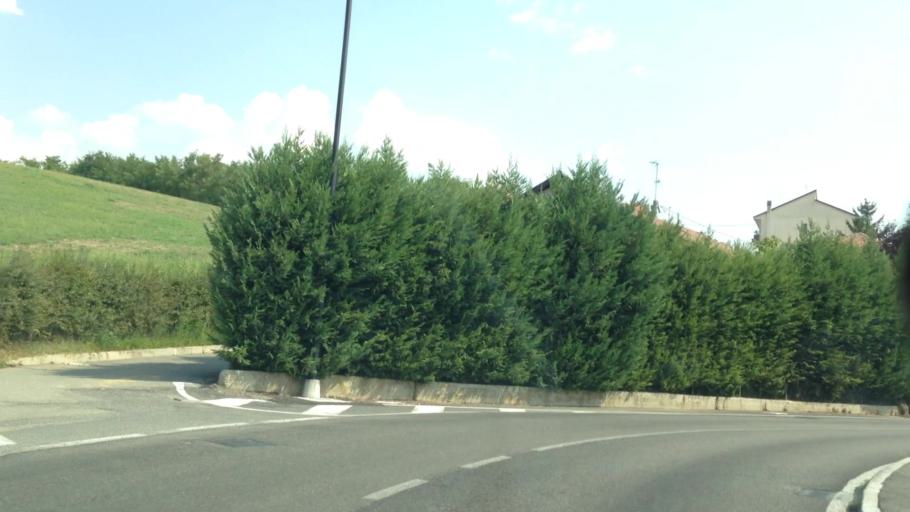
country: IT
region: Piedmont
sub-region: Provincia di Asti
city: Asti
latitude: 44.9094
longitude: 8.1844
